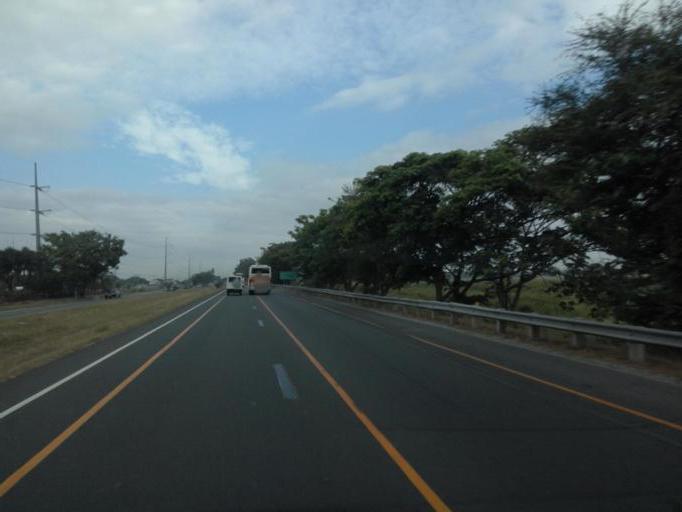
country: PH
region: Central Luzon
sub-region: Province of Pampanga
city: Pau
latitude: 15.0309
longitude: 120.7162
